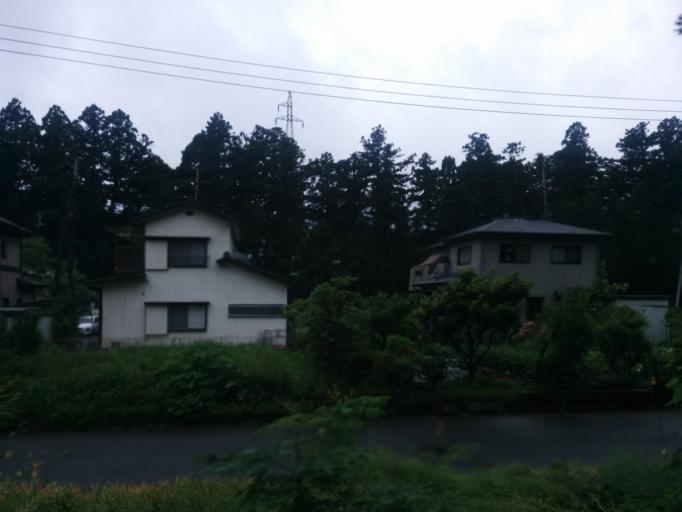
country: JP
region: Tochigi
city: Imaichi
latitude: 36.6529
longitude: 139.7229
